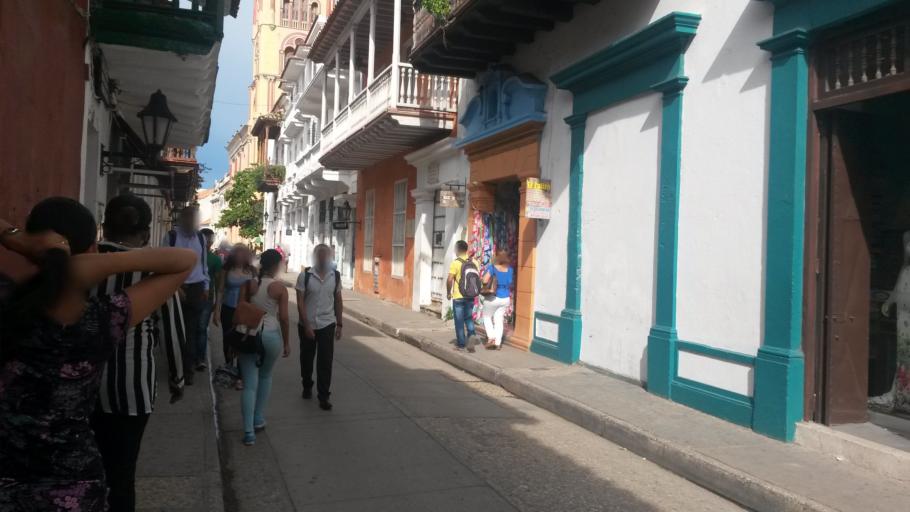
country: CO
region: Bolivar
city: Cartagena
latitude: 10.4252
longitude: -75.5488
